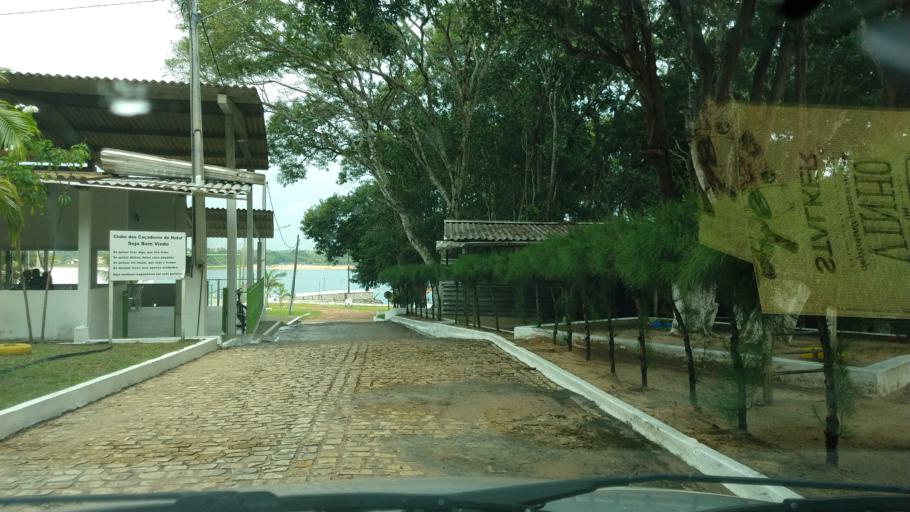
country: BR
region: Rio Grande do Norte
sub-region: Sao Jose De Mipibu
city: Sao Jose de Mipibu
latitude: -6.0346
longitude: -35.2147
